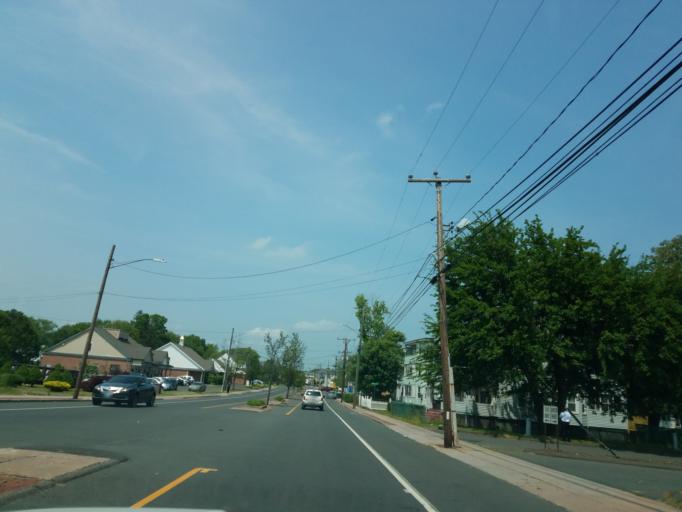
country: US
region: Connecticut
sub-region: Hartford County
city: Blue Hills
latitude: 41.8105
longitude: -72.6585
